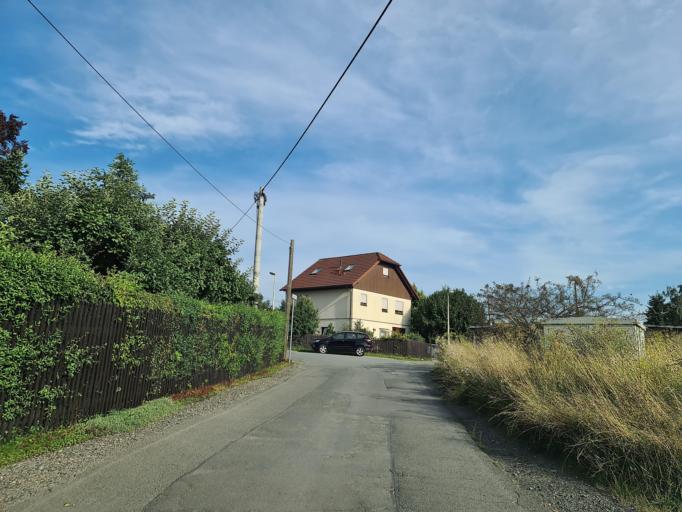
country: DE
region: Saxony
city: Plauen
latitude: 50.4908
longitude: 12.1110
